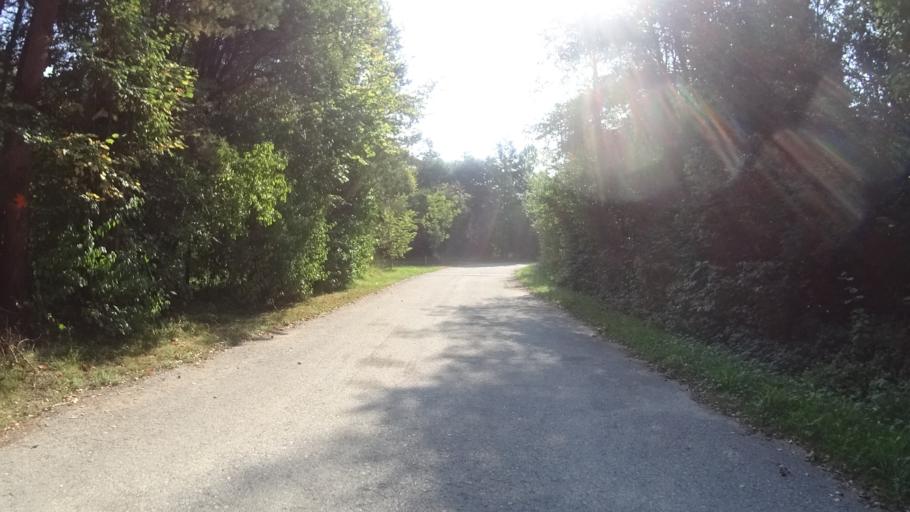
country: AT
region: Carinthia
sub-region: Politischer Bezirk Klagenfurt Land
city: Maria Rain
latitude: 46.5454
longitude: 14.2964
